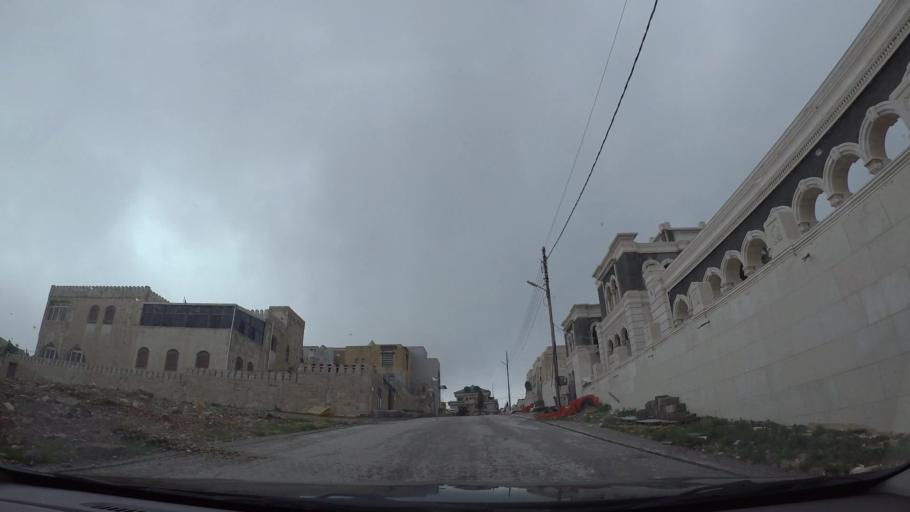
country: JO
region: Amman
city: Al Bunayyat ash Shamaliyah
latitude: 31.9451
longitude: 35.8841
